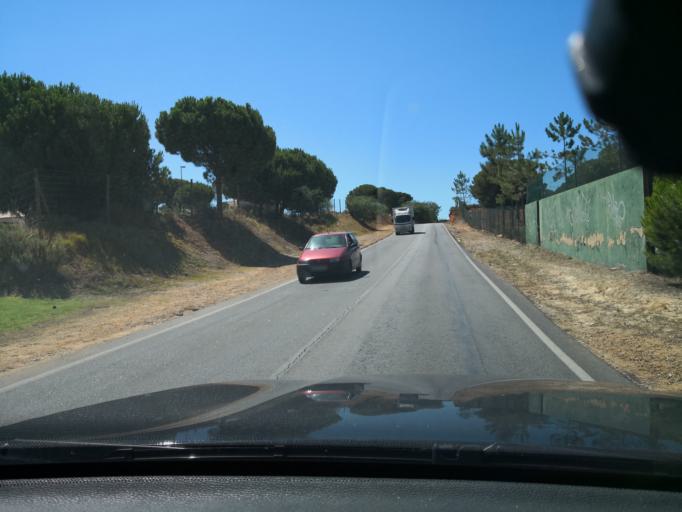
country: PT
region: Faro
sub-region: Loule
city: Vilamoura
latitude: 37.0905
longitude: -8.1021
